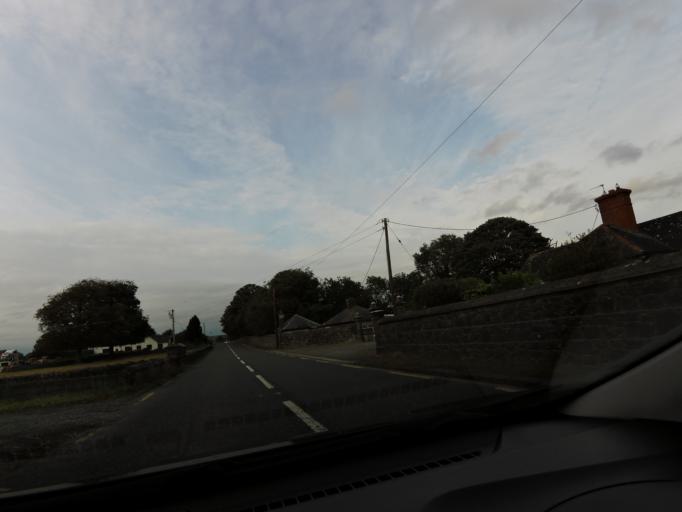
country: IE
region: Leinster
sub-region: Uibh Fhaili
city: Ferbane
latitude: 53.2873
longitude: -7.8195
